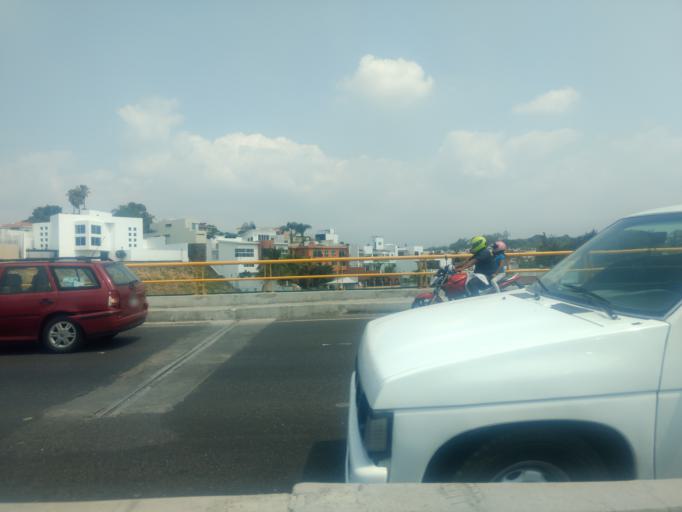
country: MX
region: Morelos
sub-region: Cuernavaca
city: Cuernavaca
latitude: 18.9001
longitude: -99.2233
